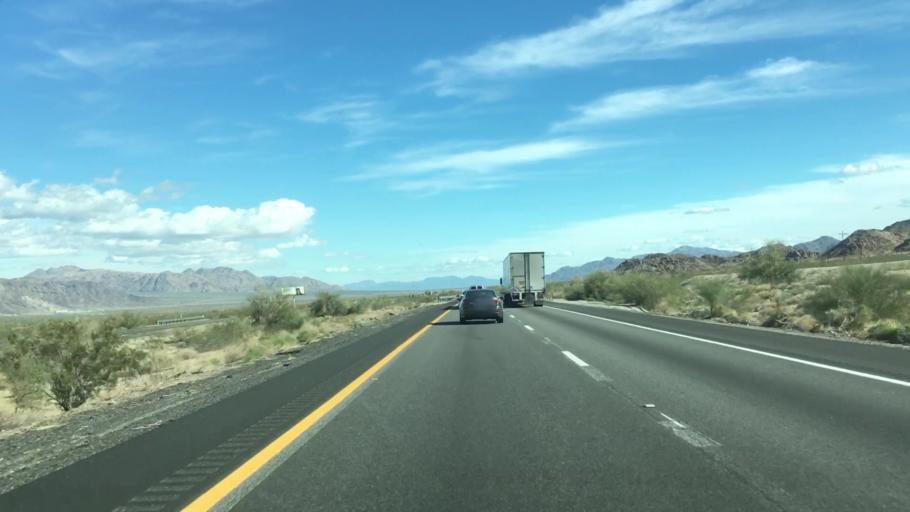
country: US
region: California
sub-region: Riverside County
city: Mecca
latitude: 33.6633
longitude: -115.7004
